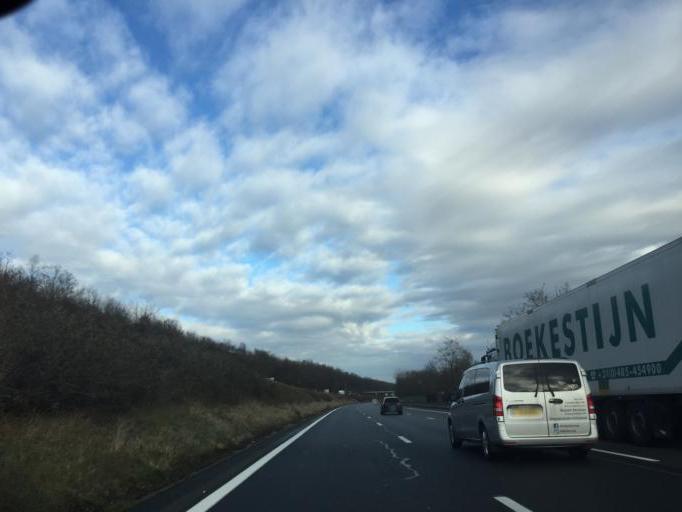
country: FR
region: Bourgogne
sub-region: Departement de Saone-et-Loire
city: Sance
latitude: 46.3385
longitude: 4.8216
